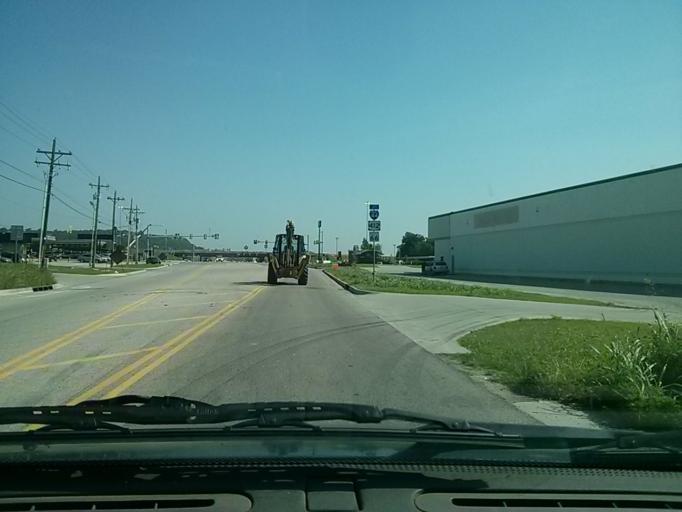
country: US
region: Oklahoma
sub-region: Rogers County
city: Catoosa
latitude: 36.1589
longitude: -95.7616
